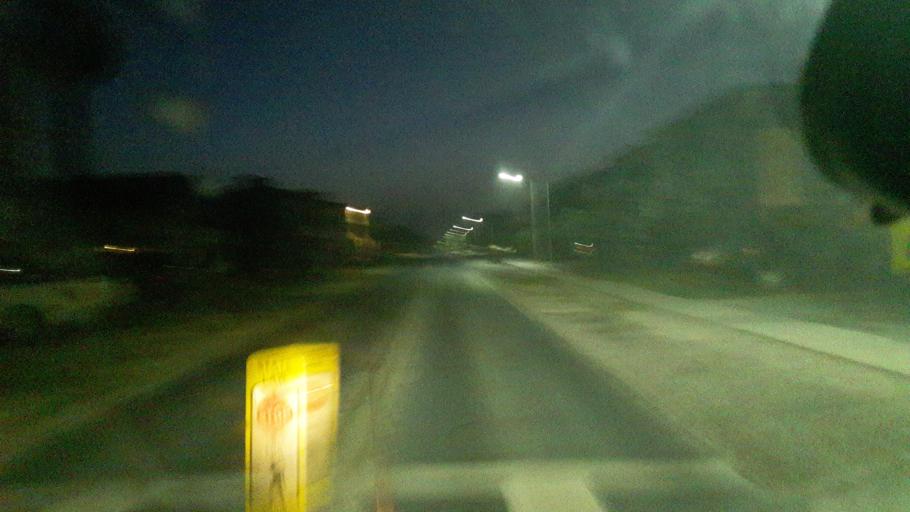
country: US
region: North Carolina
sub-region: Brunswick County
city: Sunset Beach
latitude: 33.8885
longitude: -78.4331
